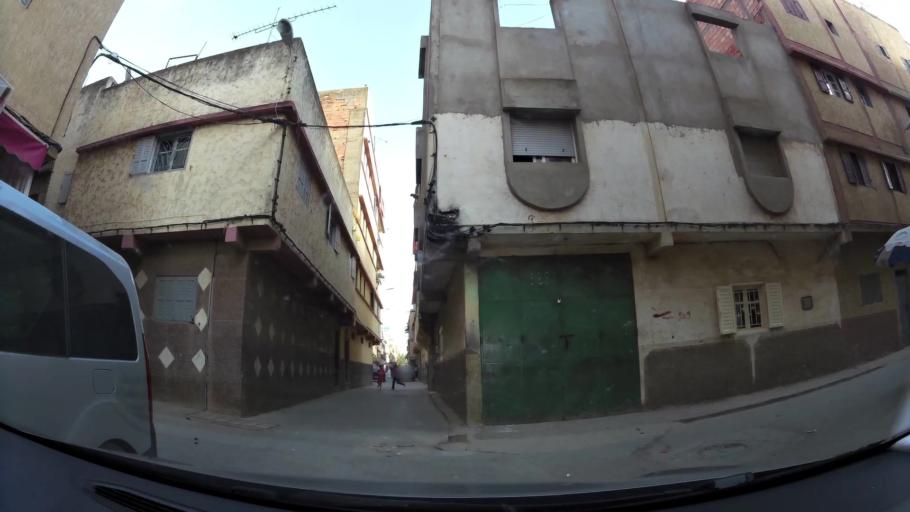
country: MA
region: Rabat-Sale-Zemmour-Zaer
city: Sale
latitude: 34.0551
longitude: -6.7756
